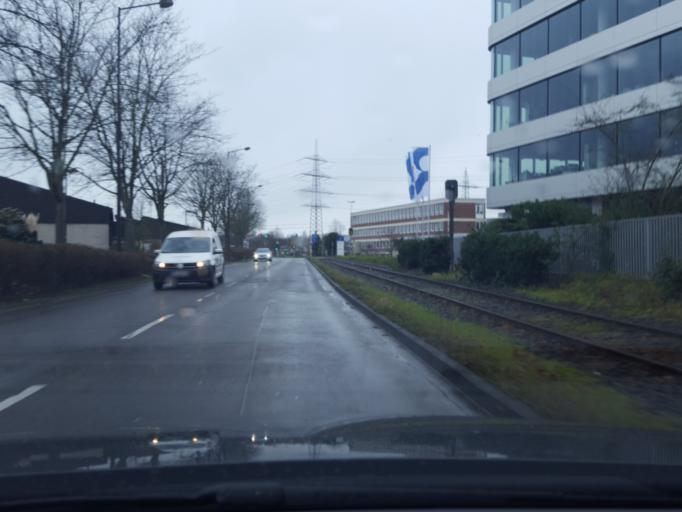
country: DE
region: North Rhine-Westphalia
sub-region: Regierungsbezirk Koln
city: Troisdorf
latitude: 50.8079
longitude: 7.1253
